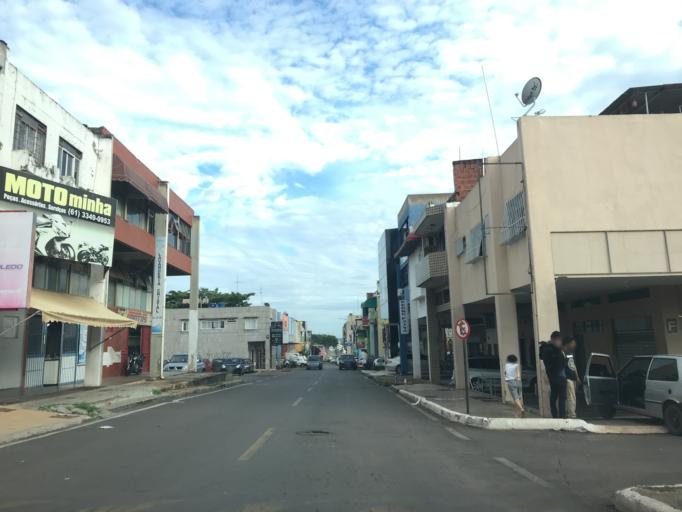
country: BR
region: Federal District
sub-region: Brasilia
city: Brasilia
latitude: -15.7655
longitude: -47.8911
